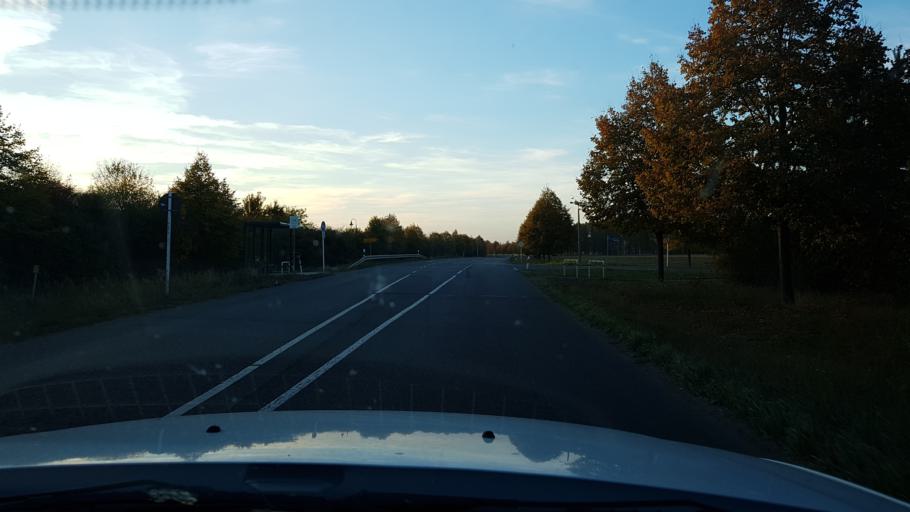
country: DE
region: Brandenburg
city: Schwedt (Oder)
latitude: 53.1020
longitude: 14.3141
